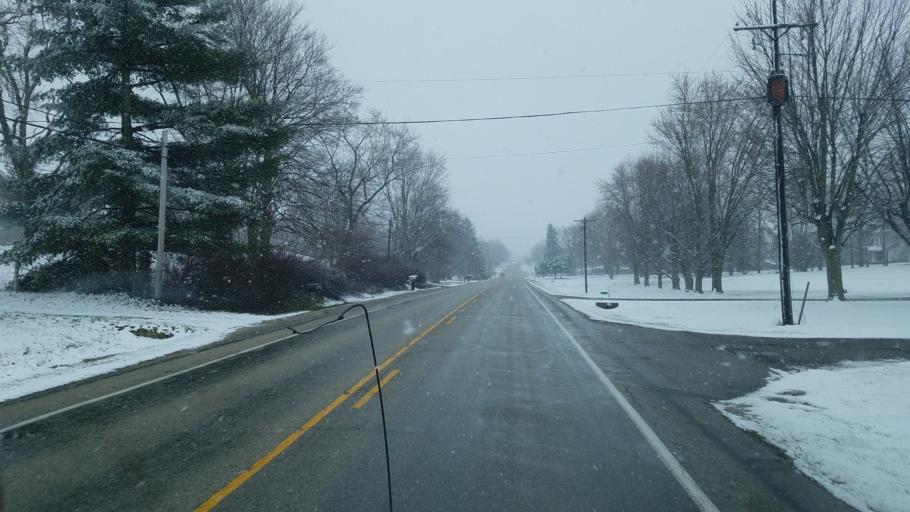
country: US
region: Indiana
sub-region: Wayne County
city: Richmond
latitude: 39.8946
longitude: -84.9442
